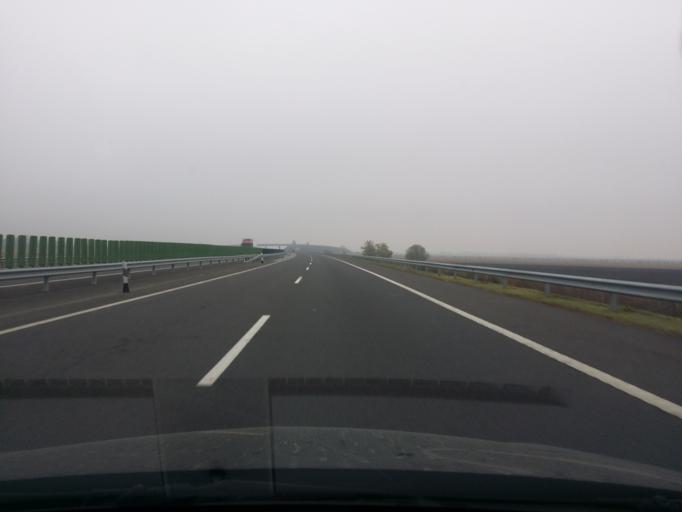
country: HU
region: Hajdu-Bihar
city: Gorbehaza
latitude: 47.7956
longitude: 21.2772
